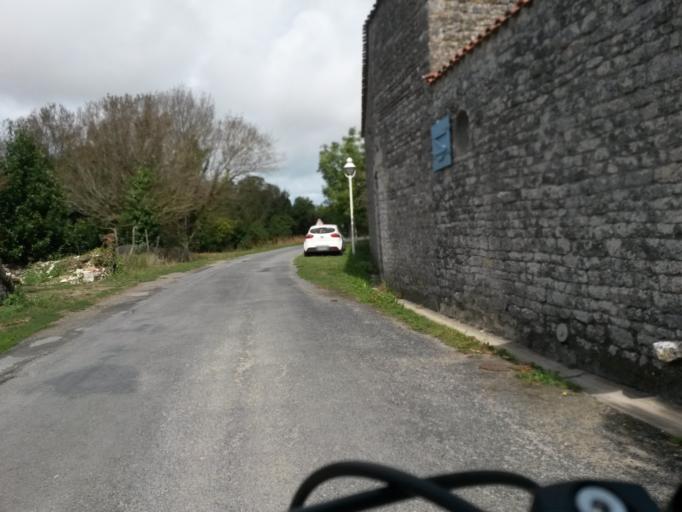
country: FR
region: Poitou-Charentes
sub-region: Departement de la Charente-Maritime
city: Dolus-d'Oleron
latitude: 45.9448
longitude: -1.2890
